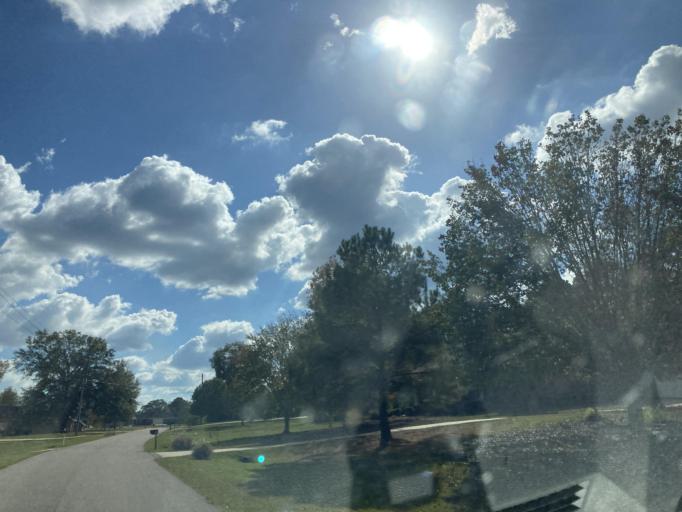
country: US
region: Mississippi
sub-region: Lamar County
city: Sumrall
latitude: 31.3986
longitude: -89.5392
